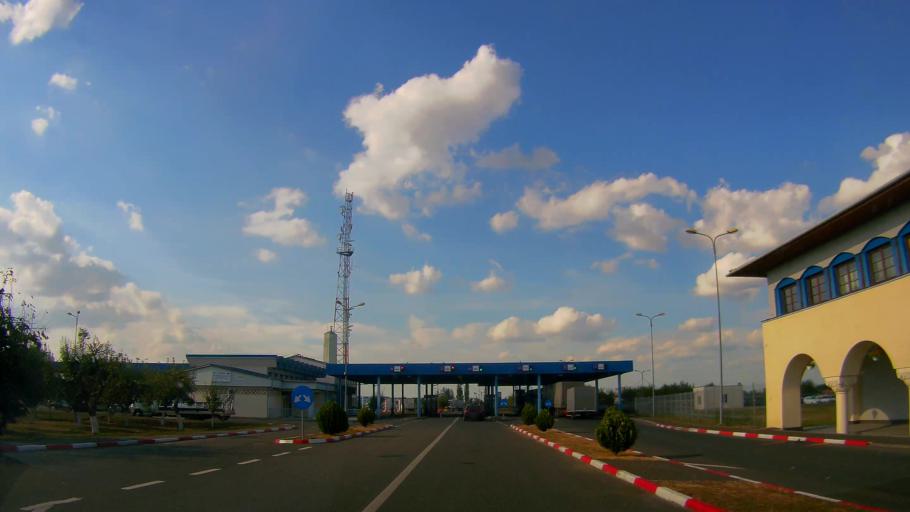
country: RO
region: Satu Mare
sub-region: Comuna Porumbesti
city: Porumbesti
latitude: 47.9916
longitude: 23.0037
